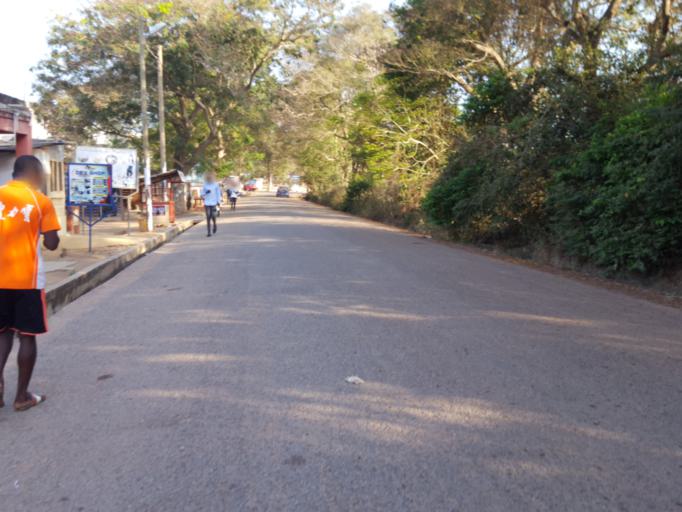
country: GH
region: Central
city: Cape Coast
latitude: 5.1140
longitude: -1.2915
